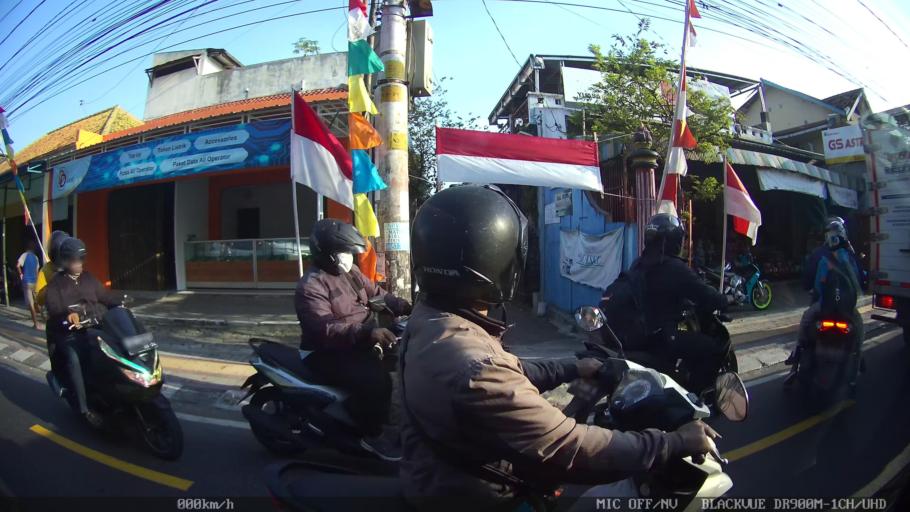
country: ID
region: Daerah Istimewa Yogyakarta
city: Yogyakarta
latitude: -7.8159
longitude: 110.3770
